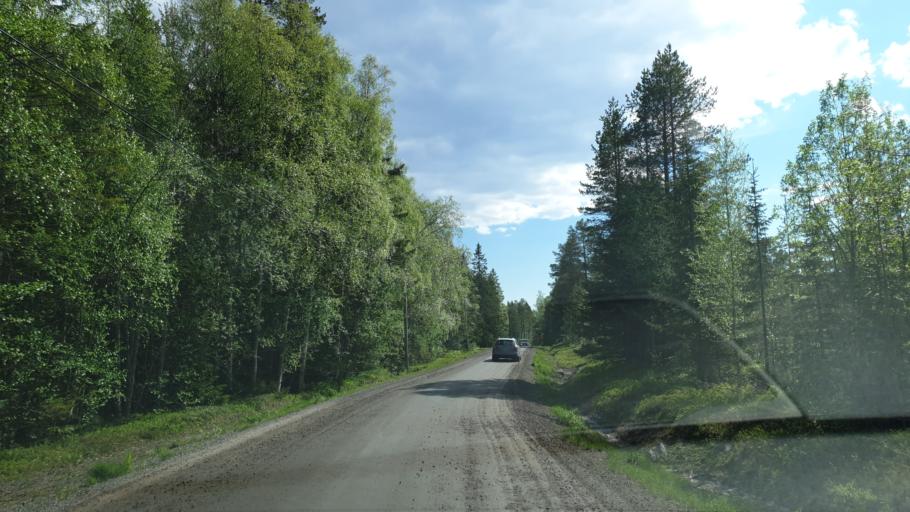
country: SE
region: Vaesterbotten
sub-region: Robertsfors Kommun
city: Robertsfors
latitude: 63.9981
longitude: 20.8912
